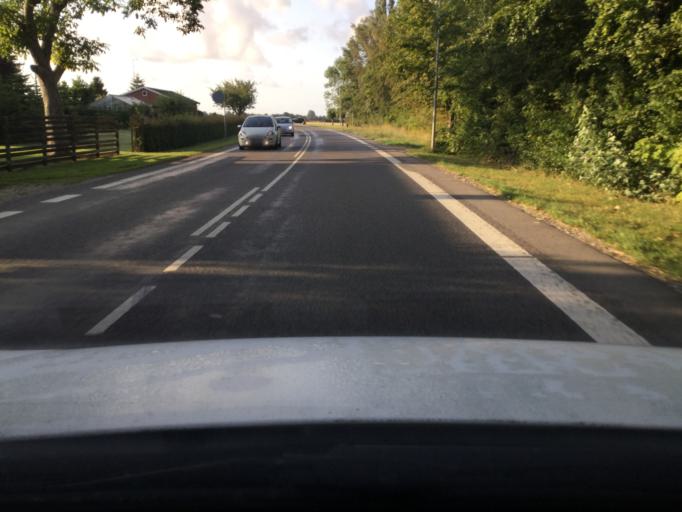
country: DK
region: Zealand
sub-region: Lolland Kommune
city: Nakskov
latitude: 54.7992
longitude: 11.2732
